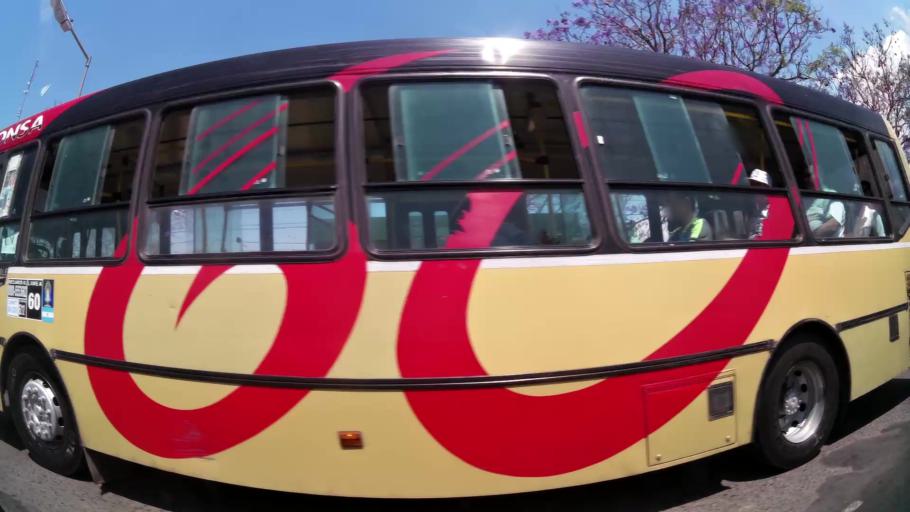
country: AR
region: Buenos Aires
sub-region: Partido de Tigre
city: Tigre
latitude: -34.4497
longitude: -58.6090
